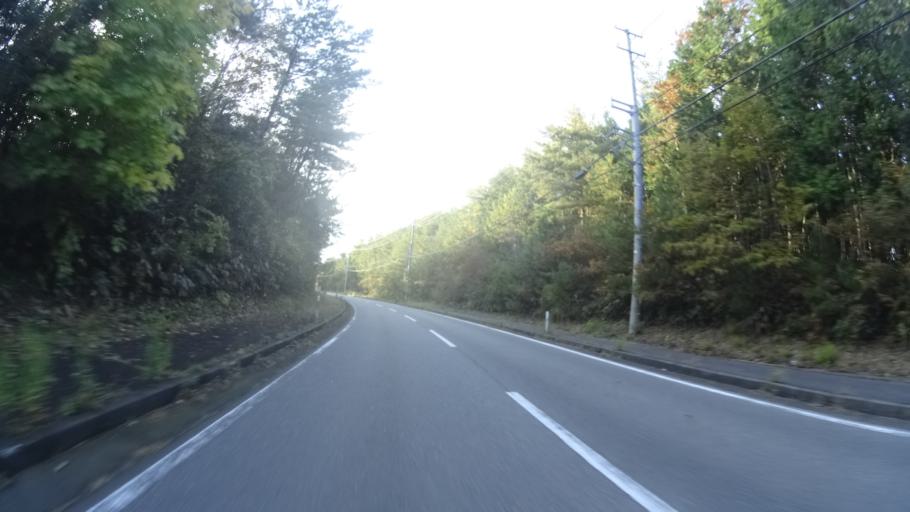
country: JP
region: Ishikawa
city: Hakui
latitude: 37.0671
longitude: 136.7645
